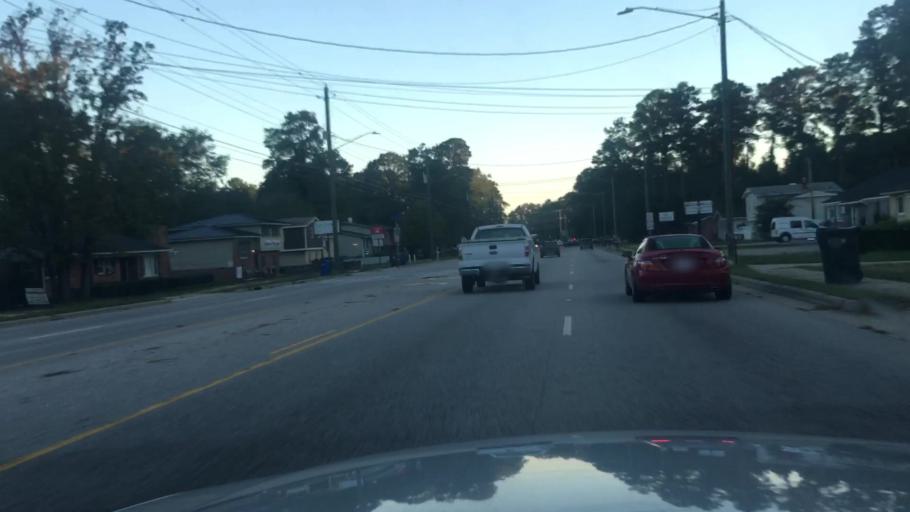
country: US
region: North Carolina
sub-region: Cumberland County
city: Hope Mills
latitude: 35.0200
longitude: -78.9626
